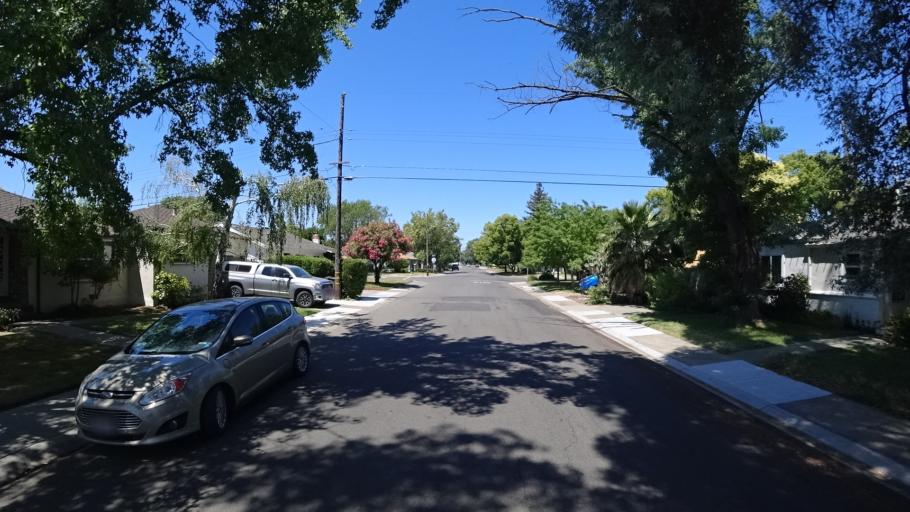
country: US
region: California
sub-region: Sacramento County
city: Parkway
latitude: 38.5422
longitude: -121.4399
